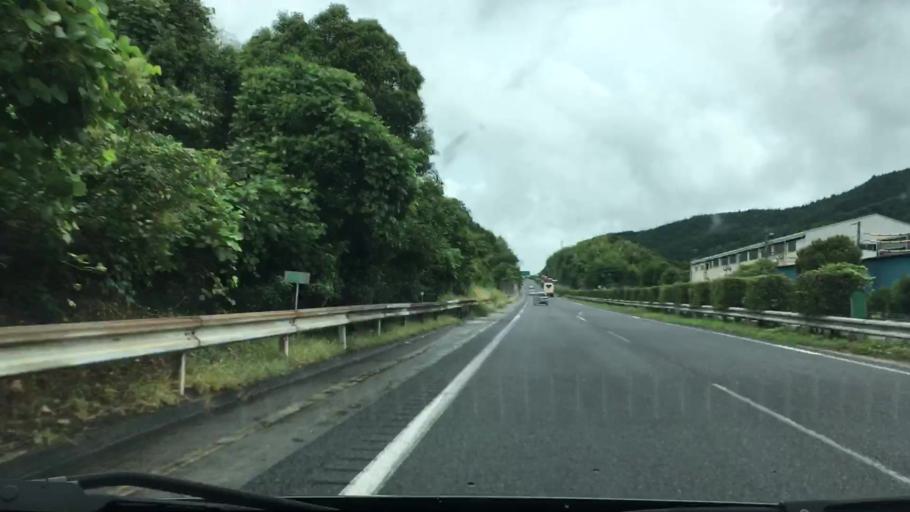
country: JP
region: Hyogo
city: Yamazakicho-nakabirose
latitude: 34.9730
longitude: 134.6569
